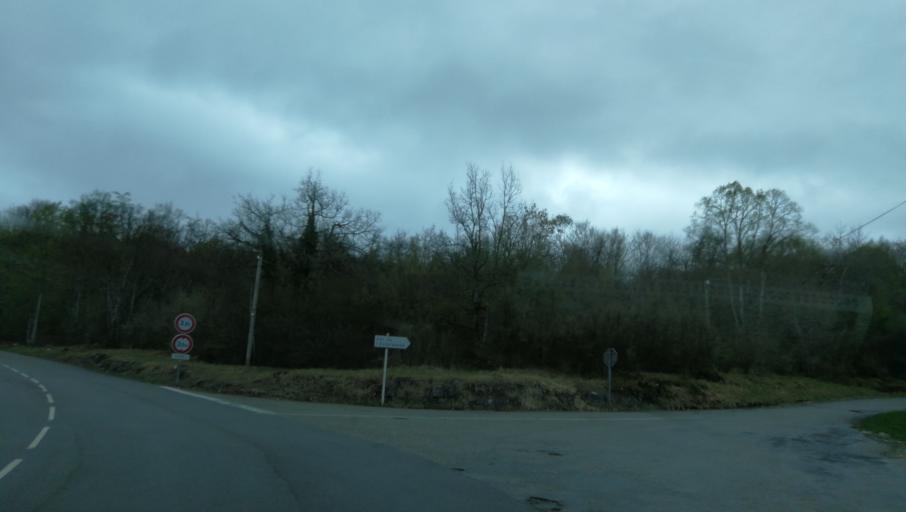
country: FR
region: Rhone-Alpes
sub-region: Departement de la Drome
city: Saint-Laurent-en-Royans
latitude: 45.0032
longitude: 5.3203
